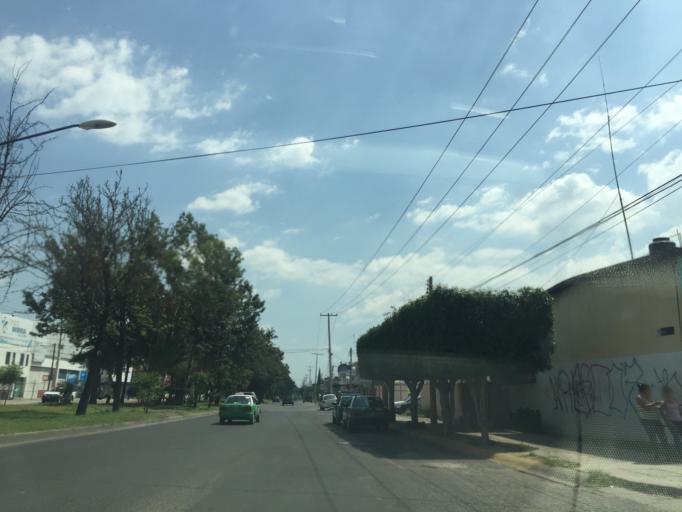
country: MX
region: Guanajuato
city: Leon
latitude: 21.1713
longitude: -101.6643
